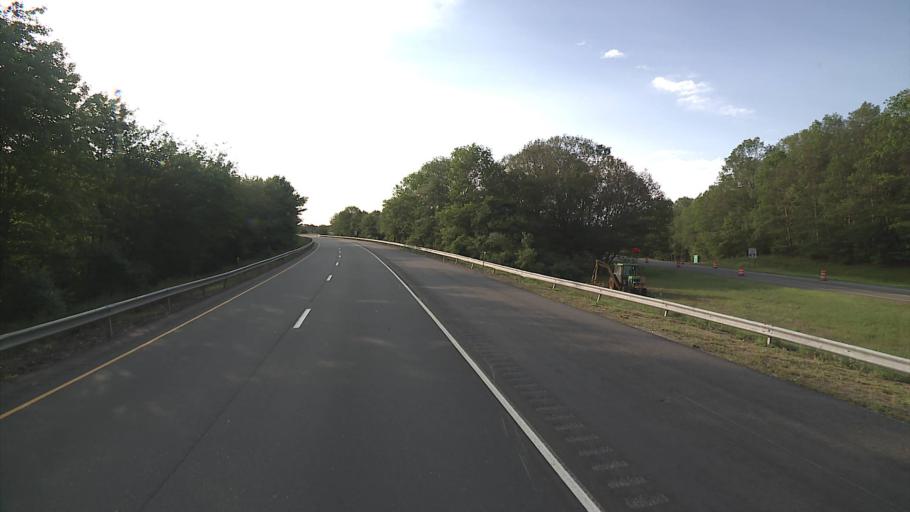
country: US
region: Connecticut
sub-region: New London County
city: Colchester
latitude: 41.5633
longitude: -72.3273
